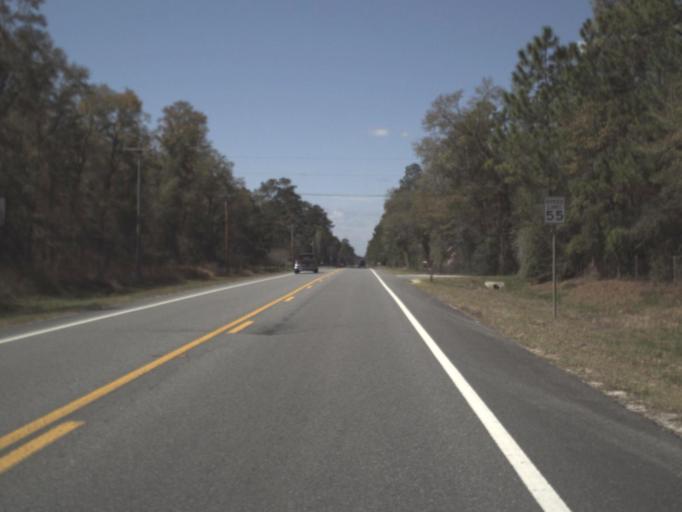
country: US
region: Florida
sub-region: Wakulla County
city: Crawfordville
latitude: 30.2530
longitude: -84.3256
